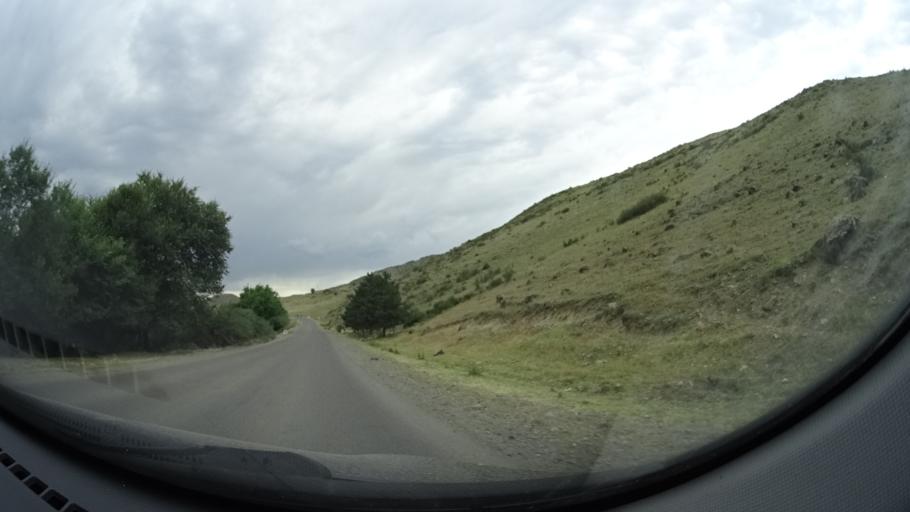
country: GE
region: Samtskhe-Javakheti
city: Aspindza
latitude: 41.5979
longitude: 43.1533
